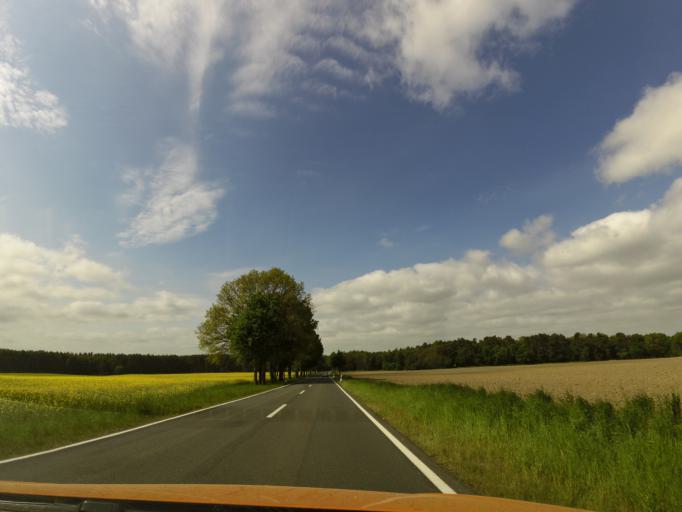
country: DE
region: Brandenburg
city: Gorzke
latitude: 52.0994
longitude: 12.3477
